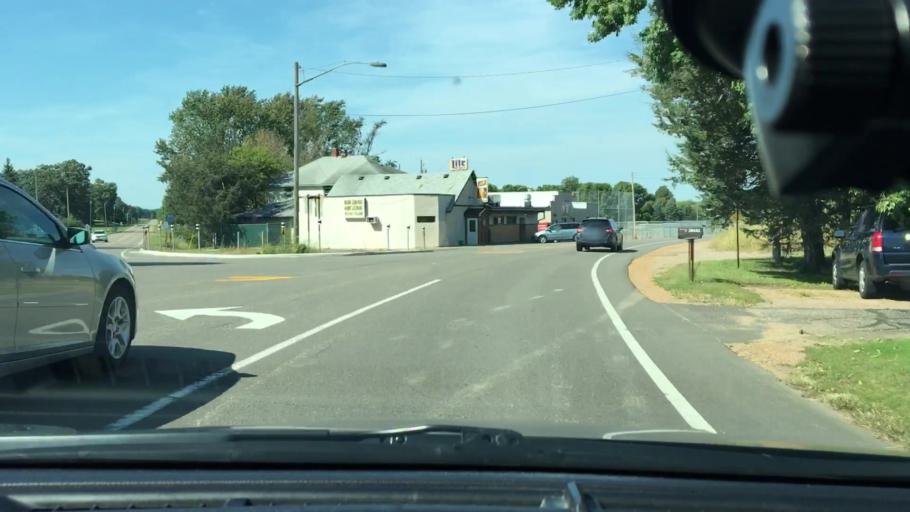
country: US
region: Minnesota
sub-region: Hennepin County
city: Corcoran
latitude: 45.0950
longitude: -93.5478
